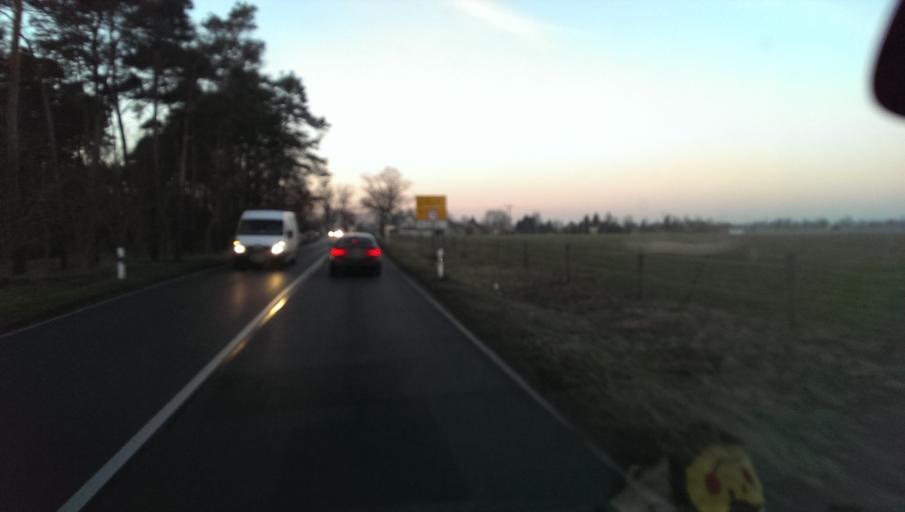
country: DE
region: Saxony-Anhalt
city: Holzdorf
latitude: 51.7941
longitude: 13.1808
